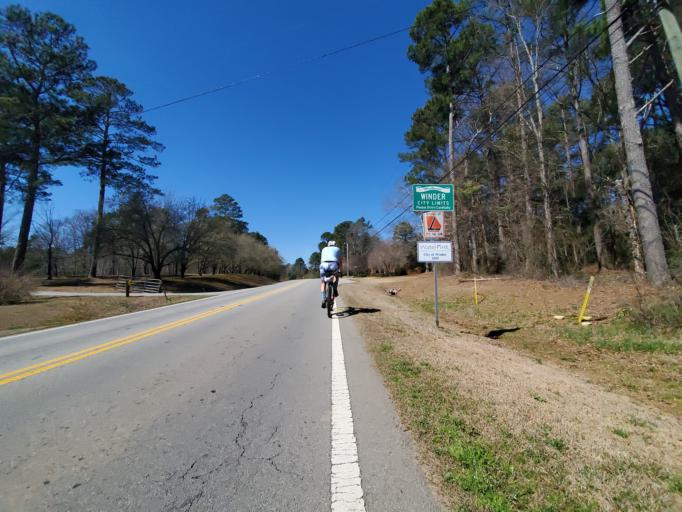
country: US
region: Georgia
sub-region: Barrow County
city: Russell
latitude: 33.9977
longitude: -83.6903
